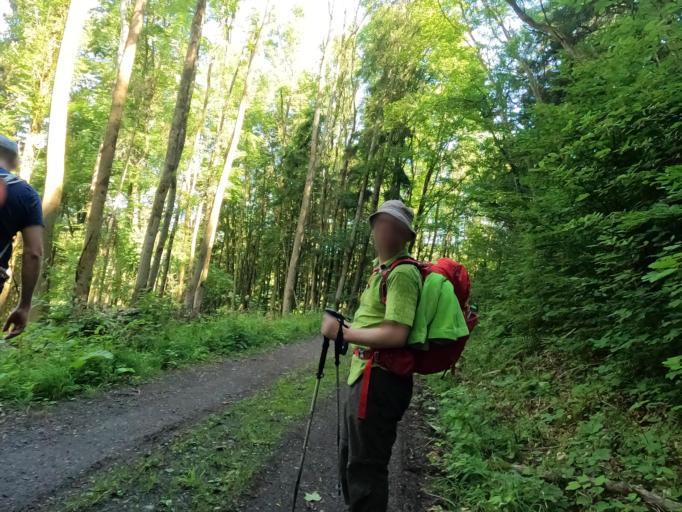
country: DE
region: Bavaria
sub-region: Regierungsbezirk Unterfranken
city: Zeitlofs
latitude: 50.3280
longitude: 9.6354
